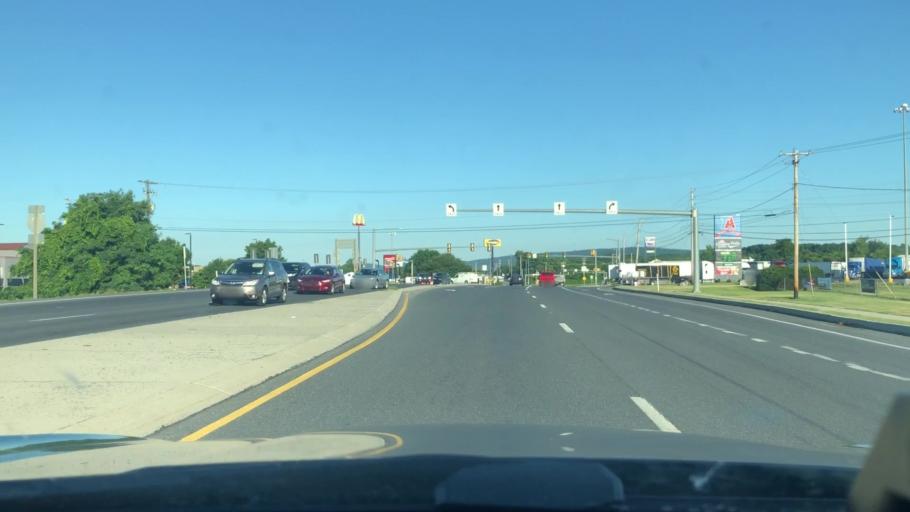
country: US
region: Pennsylvania
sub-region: Dauphin County
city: Skyline View
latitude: 40.3530
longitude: -76.7241
